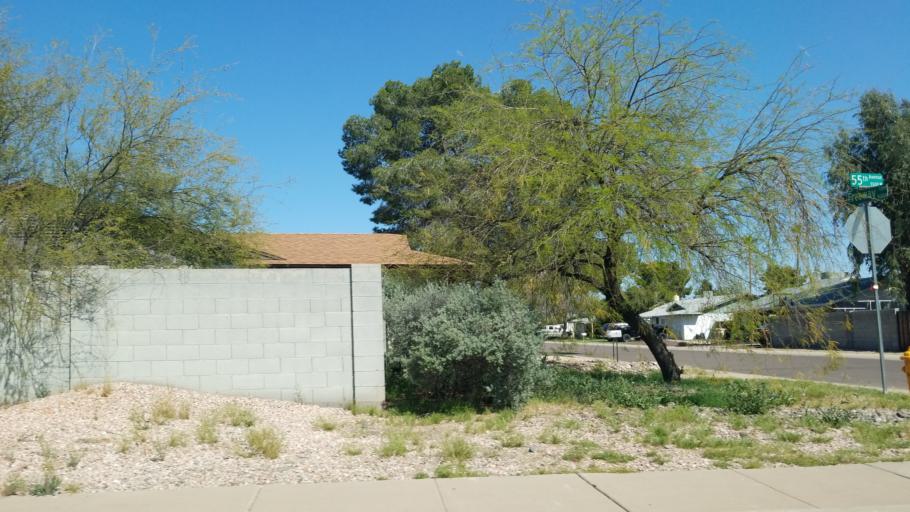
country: US
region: Arizona
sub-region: Maricopa County
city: Glendale
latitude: 33.5619
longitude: -112.1776
